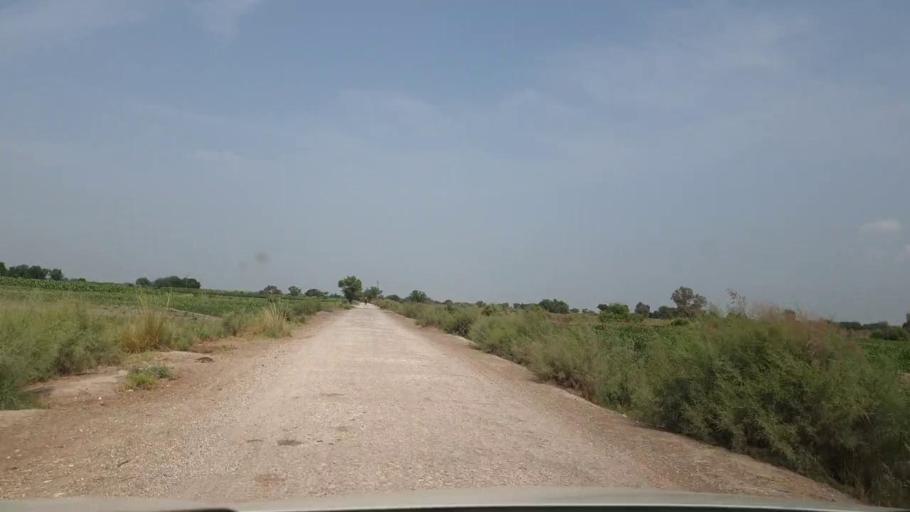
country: PK
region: Sindh
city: Sobhadero
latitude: 27.3886
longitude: 68.2725
